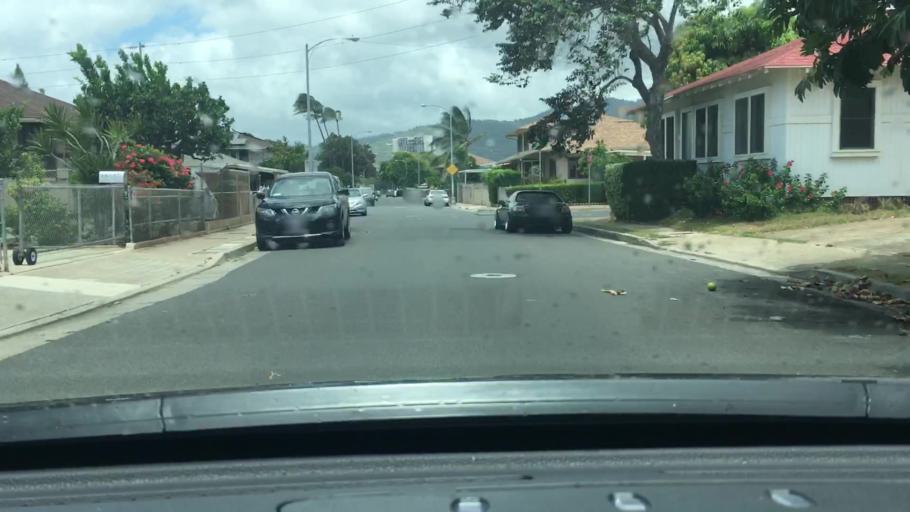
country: US
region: Hawaii
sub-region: Honolulu County
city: Honolulu
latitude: 21.2715
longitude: -157.8136
